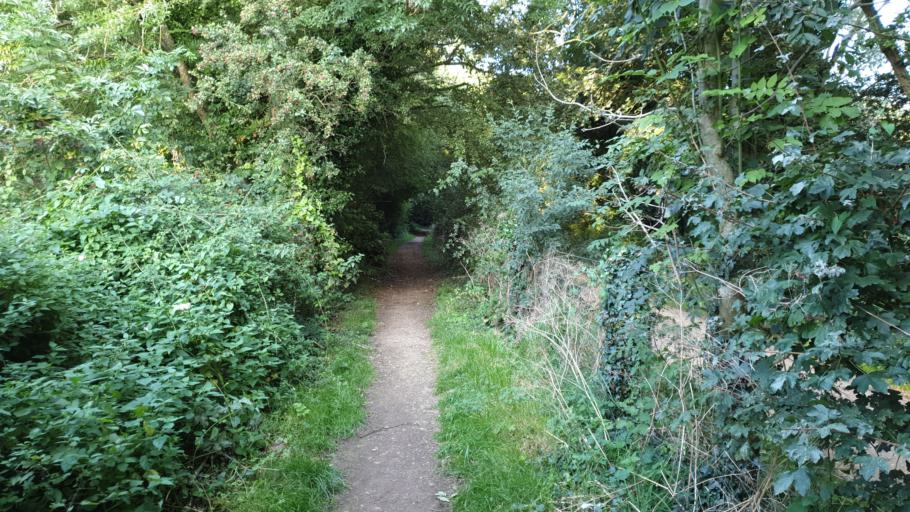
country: GB
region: England
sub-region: Wiltshire
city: Minety
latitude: 51.6450
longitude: -1.9564
